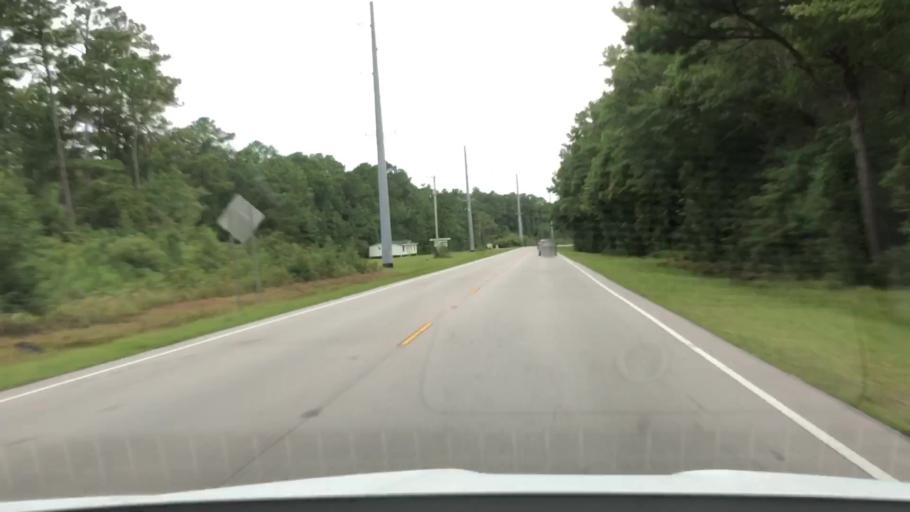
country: US
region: North Carolina
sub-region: Carteret County
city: Cape Carteret
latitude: 34.7464
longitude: -77.0902
